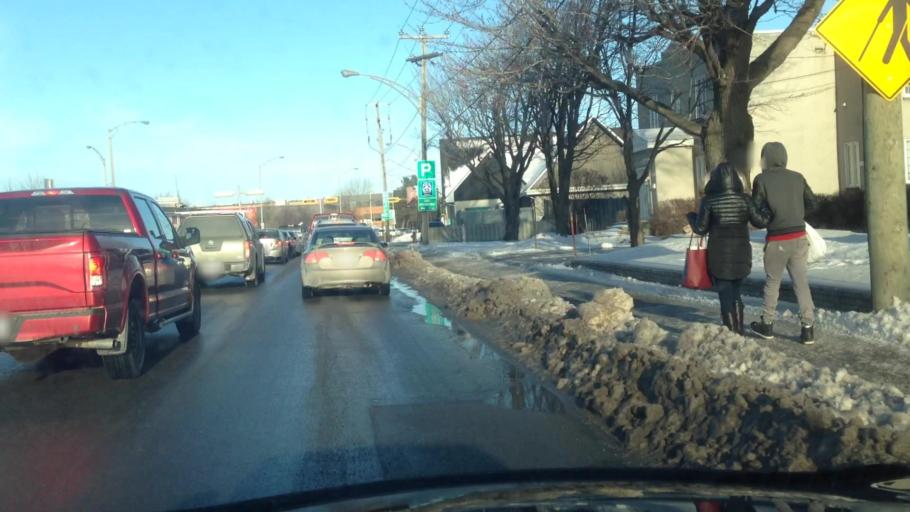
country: CA
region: Quebec
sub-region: Laurentides
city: Saint-Jerome
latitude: 45.7611
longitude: -73.9922
